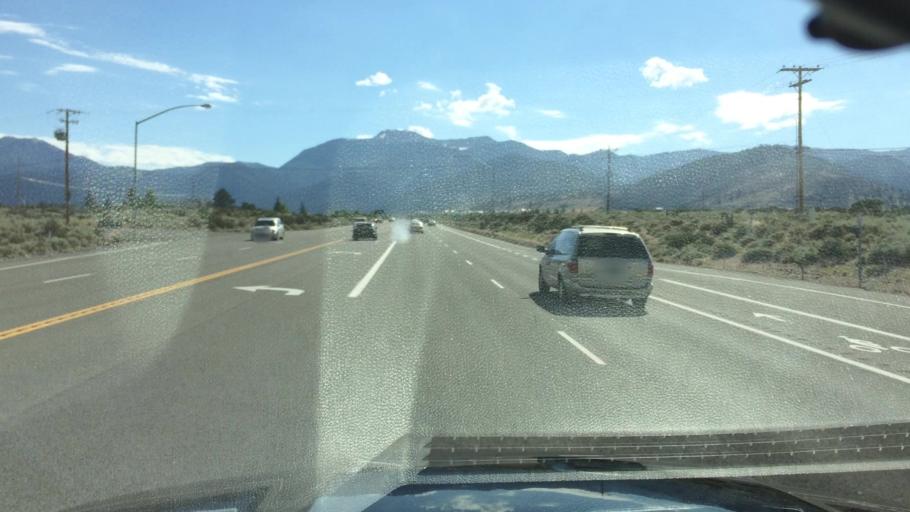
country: US
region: Nevada
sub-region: Washoe County
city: Reno
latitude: 39.3892
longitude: -119.8050
